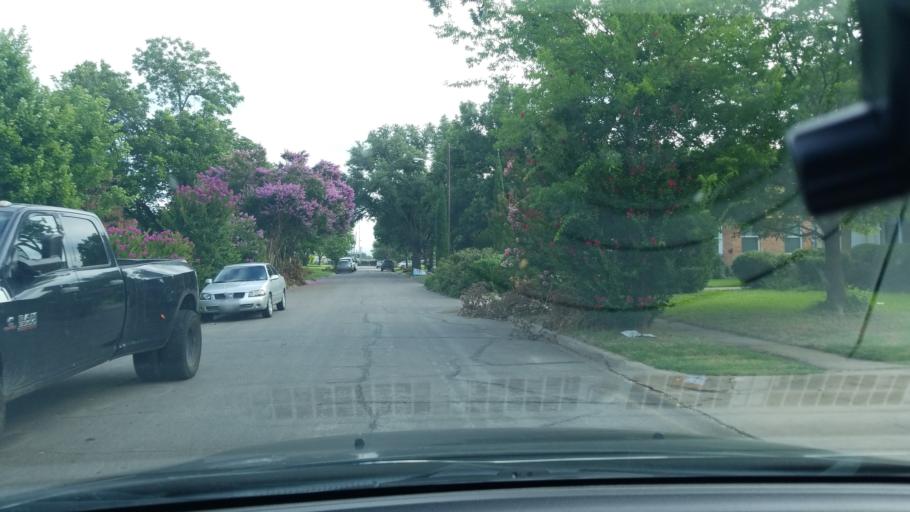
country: US
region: Texas
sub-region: Dallas County
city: Mesquite
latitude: 32.8157
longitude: -96.6787
